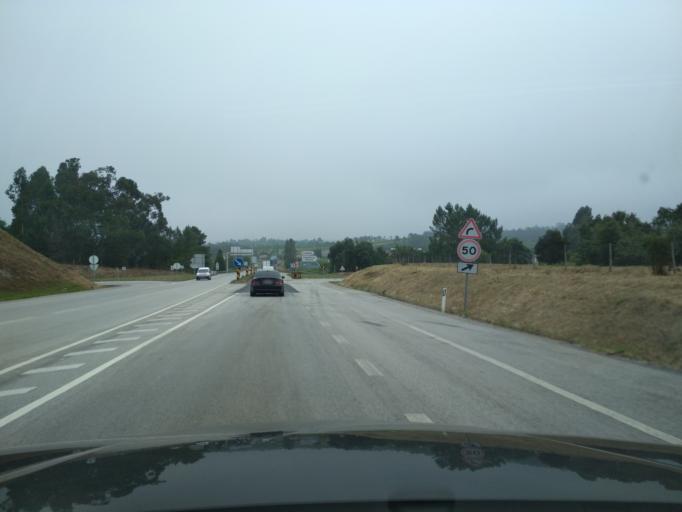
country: PT
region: Aveiro
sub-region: Mealhada
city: Mealhada
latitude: 40.3532
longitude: -8.4518
